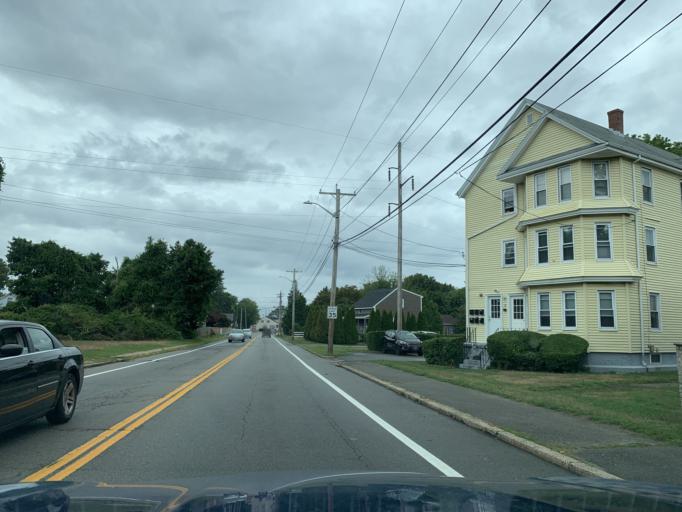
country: US
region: Rhode Island
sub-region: Bristol County
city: Warren
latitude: 41.7316
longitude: -71.2705
